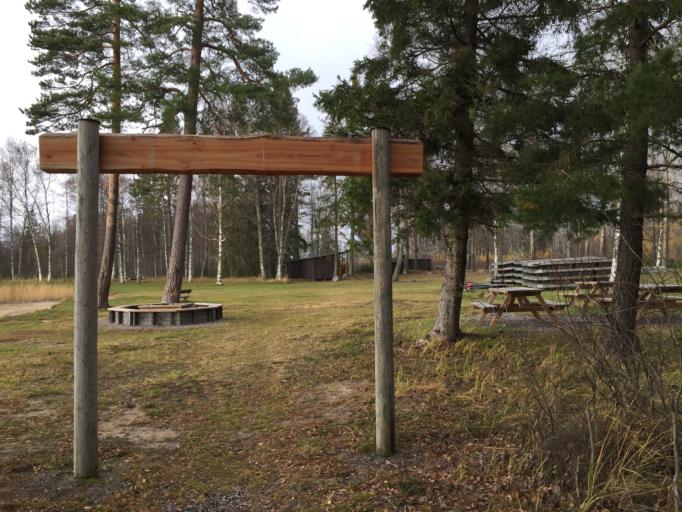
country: SE
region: OErebro
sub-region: Orebro Kommun
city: Odensbacken
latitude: 59.0526
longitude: 15.5524
